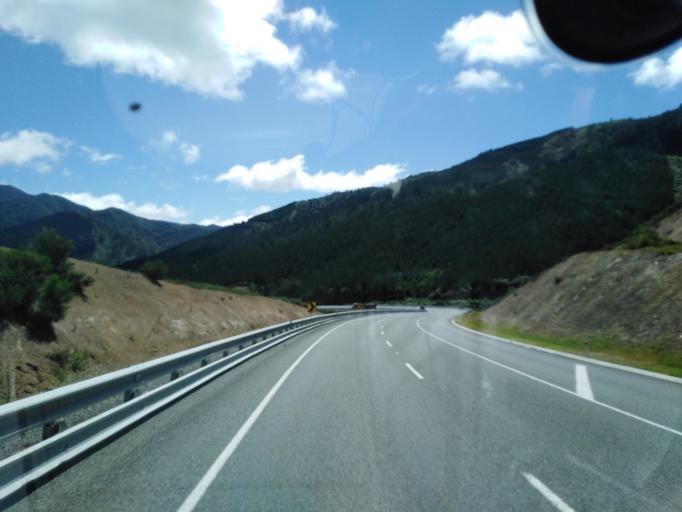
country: NZ
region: Nelson
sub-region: Nelson City
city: Nelson
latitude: -41.1860
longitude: 173.5566
